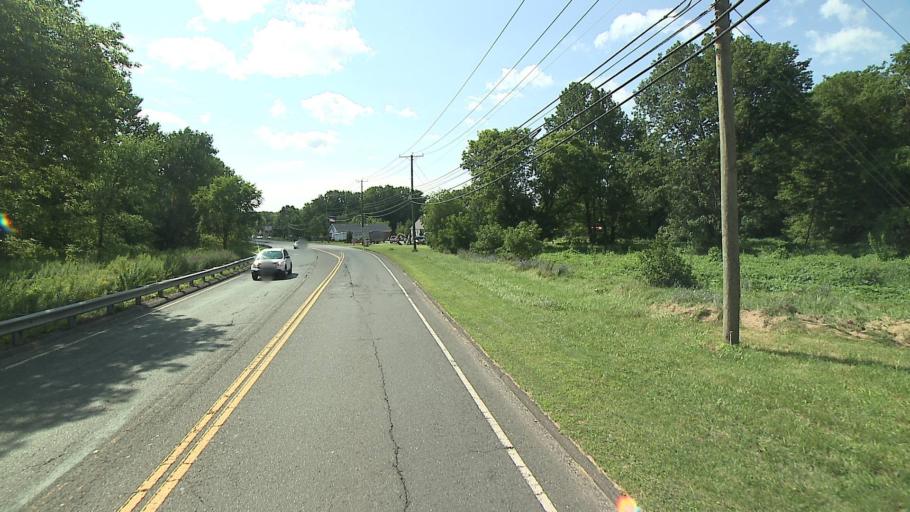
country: US
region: Connecticut
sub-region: Litchfield County
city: New Milford
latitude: 41.5763
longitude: -73.4201
